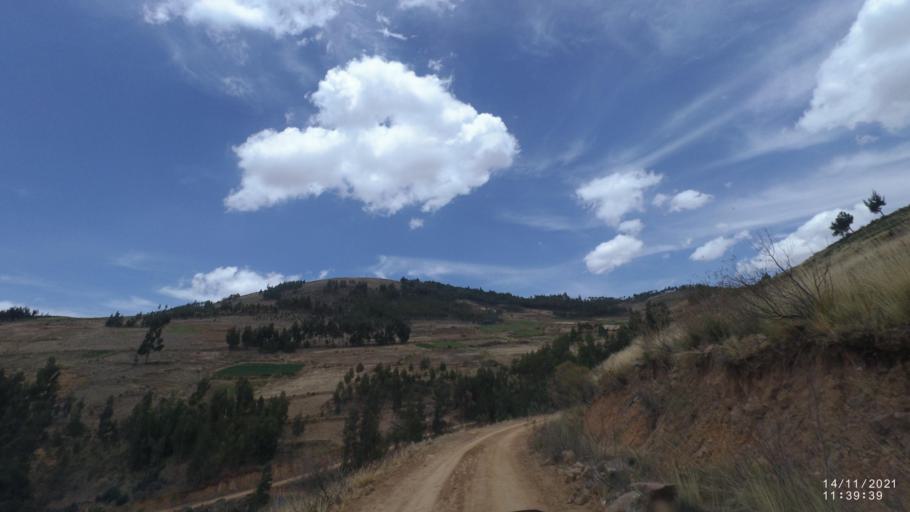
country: BO
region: Cochabamba
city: Colomi
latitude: -17.3504
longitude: -65.9959
